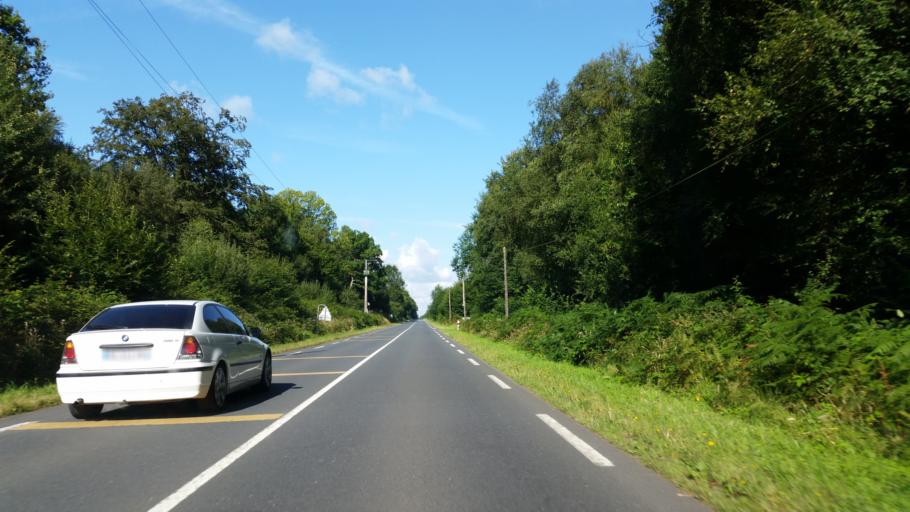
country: FR
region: Lower Normandy
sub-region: Departement du Calvados
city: Touques
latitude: 49.3421
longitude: 0.1401
